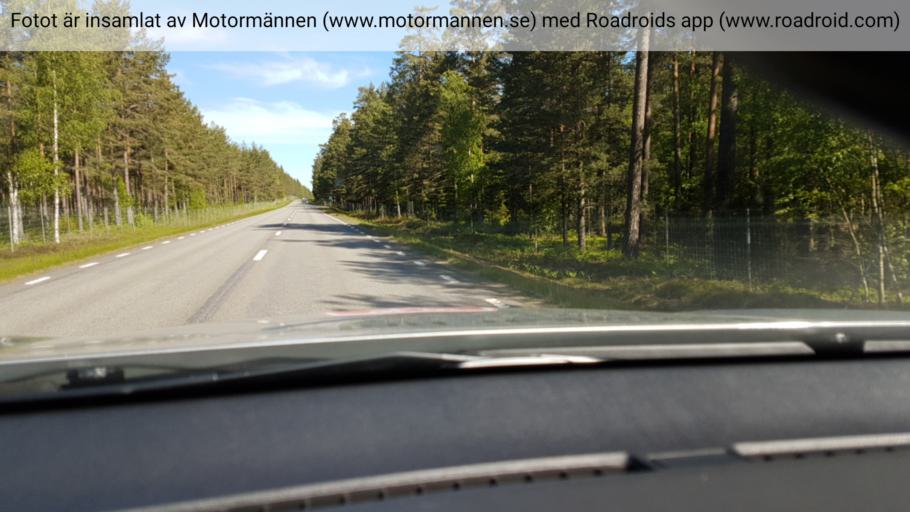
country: SE
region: Vaestra Goetaland
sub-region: Hjo Kommun
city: Hjo
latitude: 58.3676
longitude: 14.3522
